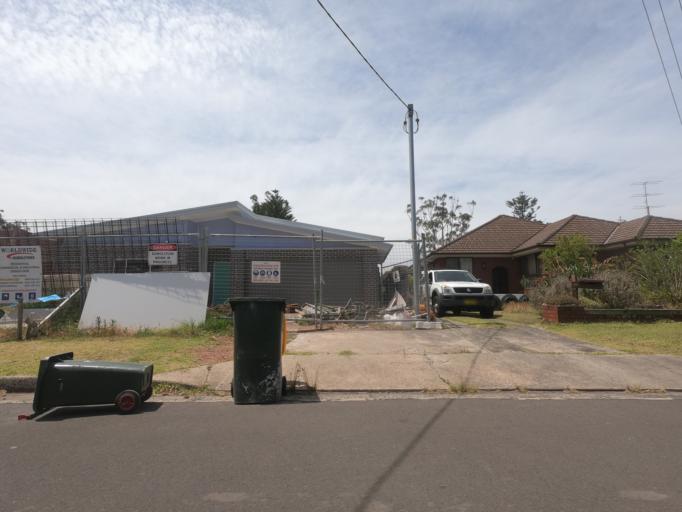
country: AU
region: New South Wales
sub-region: Wollongong
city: Mount Ousley
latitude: -34.3941
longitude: 150.8841
